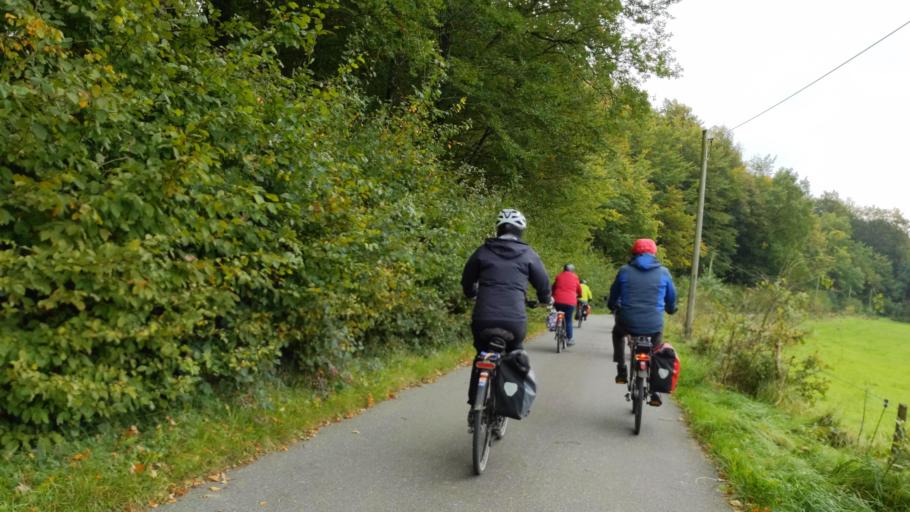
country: DE
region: Schleswig-Holstein
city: Rehhorst
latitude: 53.8614
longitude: 10.4741
